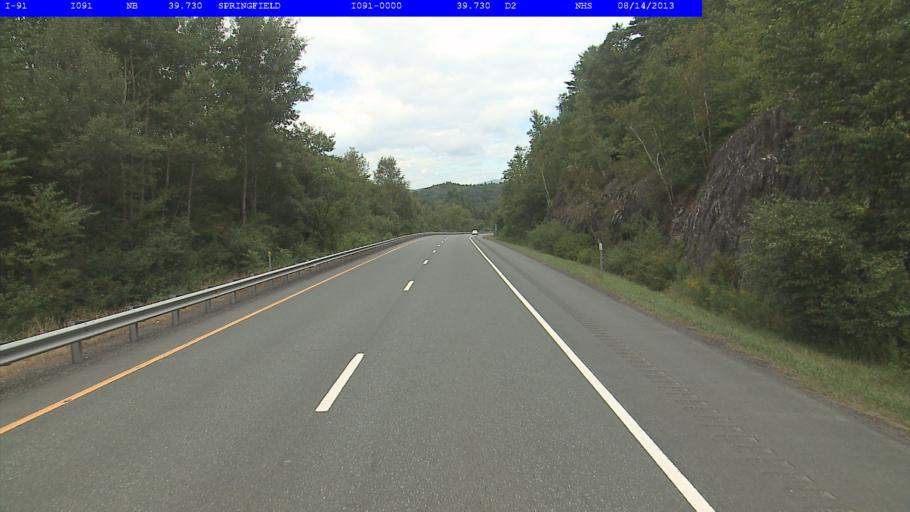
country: US
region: New Hampshire
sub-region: Sullivan County
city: Charlestown
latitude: 43.2411
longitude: -72.4480
